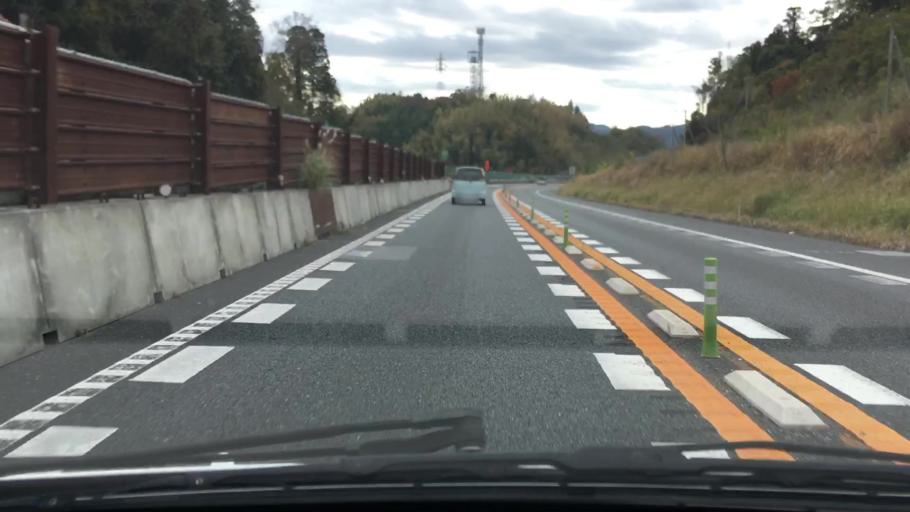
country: JP
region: Chiba
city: Kimitsu
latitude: 35.2306
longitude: 139.8868
